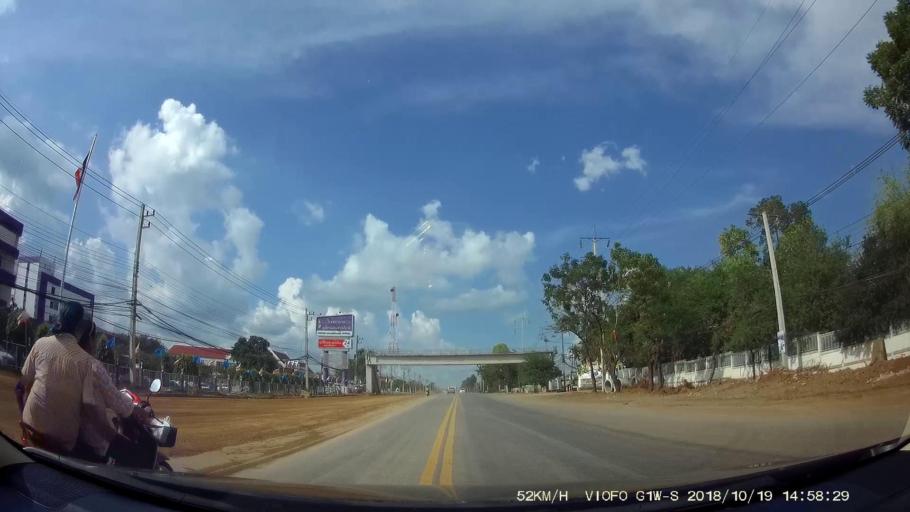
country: TH
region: Chaiyaphum
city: Phu Khiao
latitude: 16.3752
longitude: 102.1293
